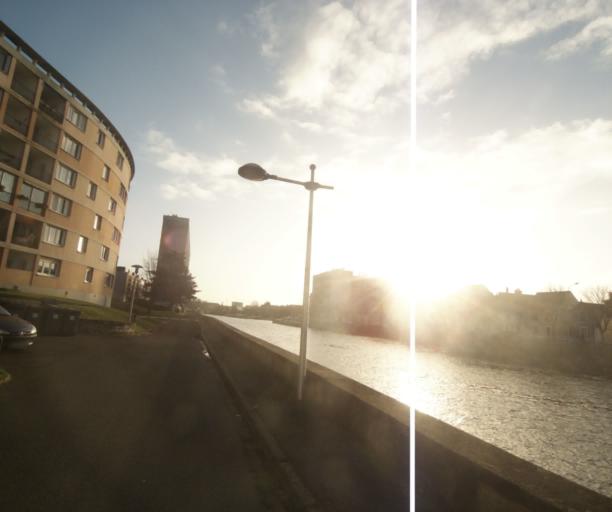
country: FR
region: Pays de la Loire
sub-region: Departement de la Sarthe
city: Le Mans
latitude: 48.0051
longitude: 0.1910
